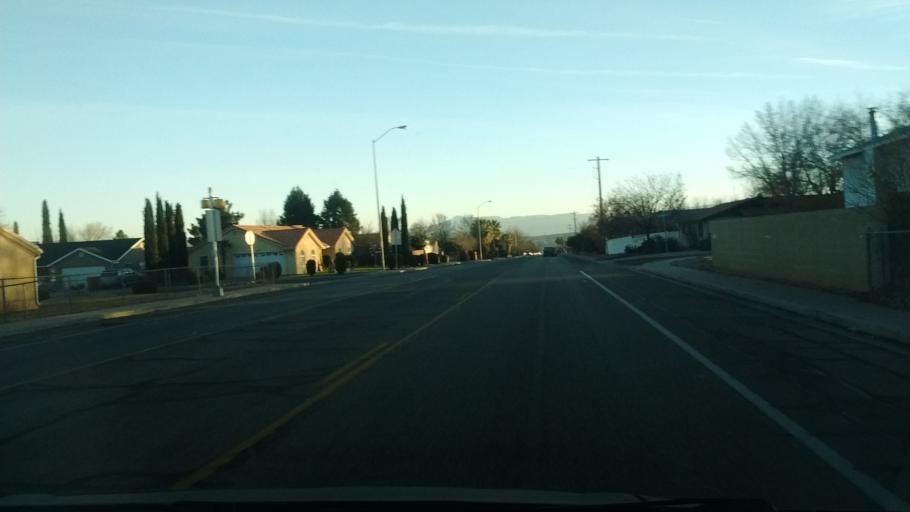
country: US
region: Utah
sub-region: Washington County
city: Washington
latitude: 37.1212
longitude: -113.5319
